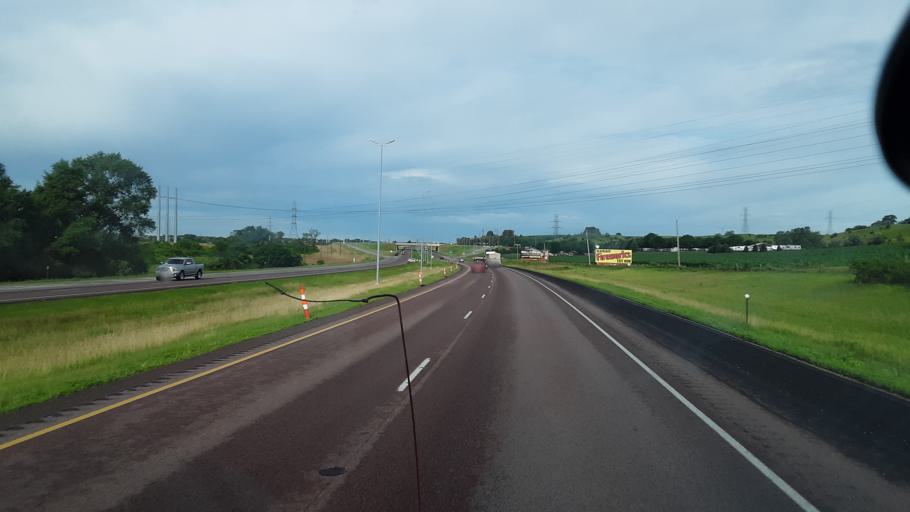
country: US
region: South Dakota
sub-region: Minnehaha County
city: Brandon
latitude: 43.6107
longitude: -96.6390
